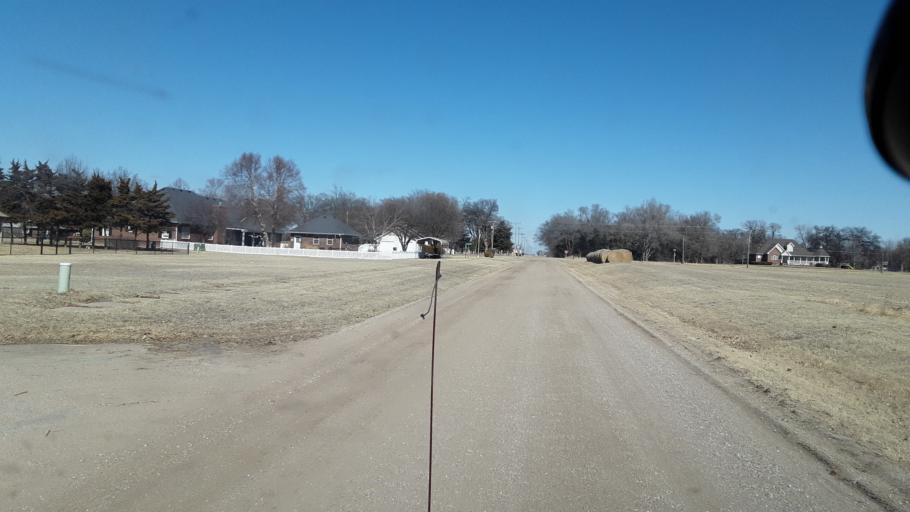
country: US
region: Kansas
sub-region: Rice County
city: Sterling
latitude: 38.2154
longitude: -98.1976
